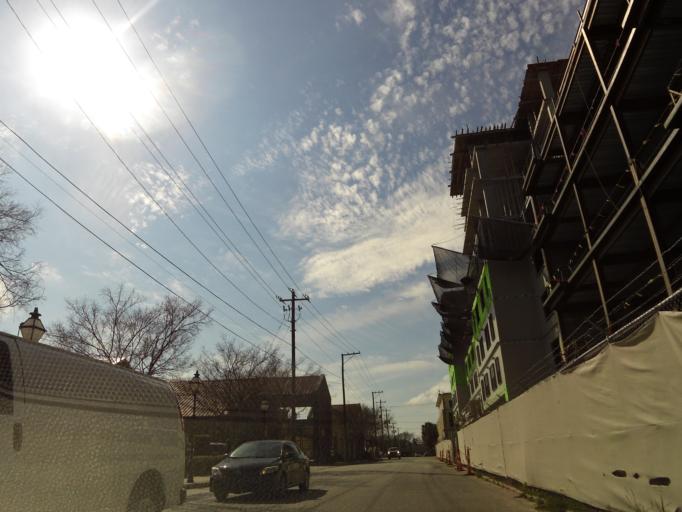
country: US
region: South Carolina
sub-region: Charleston County
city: Charleston
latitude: 32.7948
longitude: -79.9397
